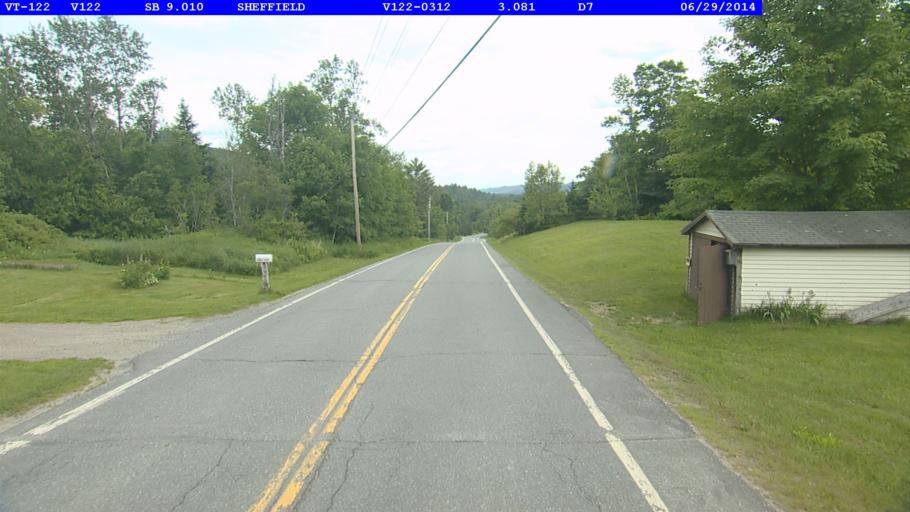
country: US
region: Vermont
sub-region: Caledonia County
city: Lyndonville
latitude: 44.6229
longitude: -72.1280
